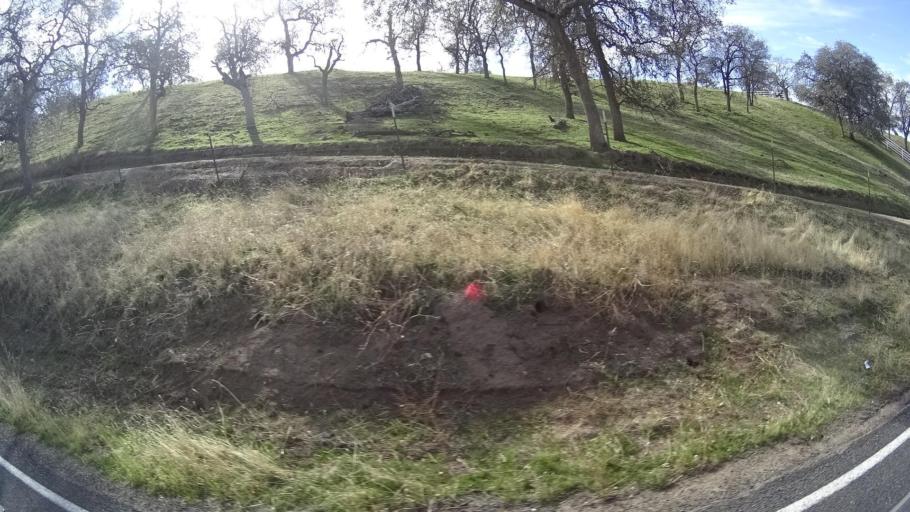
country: US
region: California
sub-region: Kern County
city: Alta Sierra
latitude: 35.6293
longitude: -118.8172
